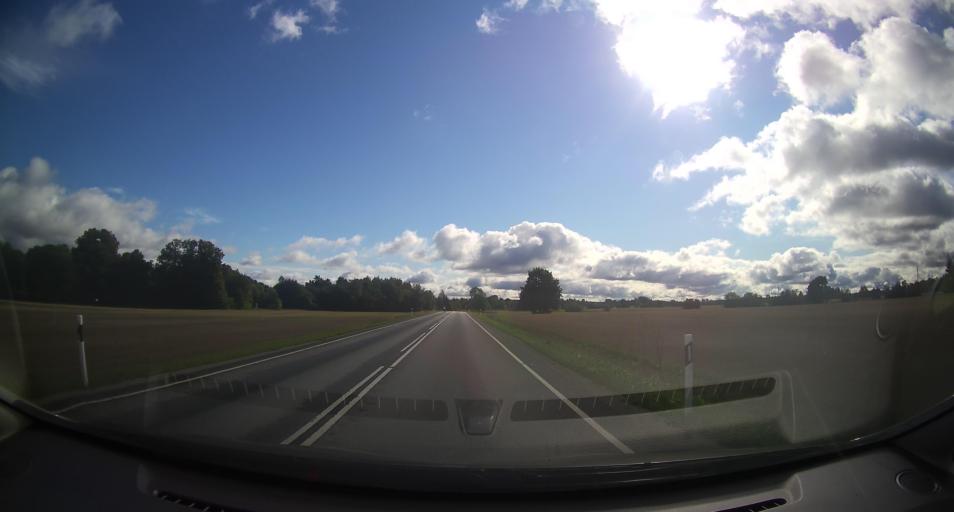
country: EE
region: Harju
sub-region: Anija vald
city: Kehra
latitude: 59.2830
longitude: 25.2464
